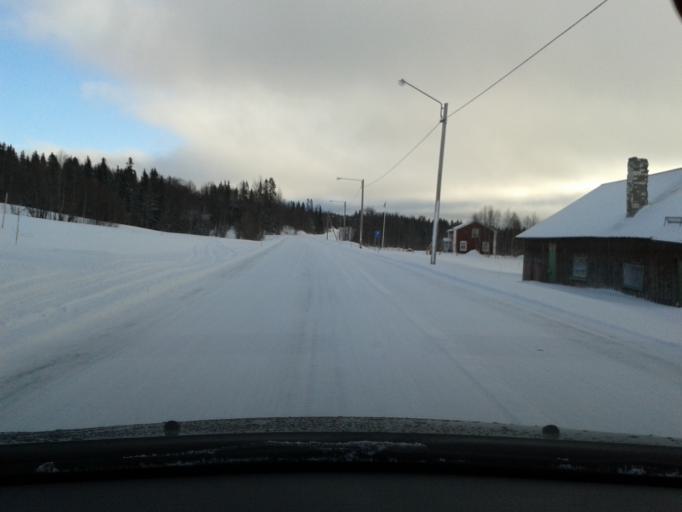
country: SE
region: Vaesterbotten
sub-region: Vilhelmina Kommun
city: Sjoberg
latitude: 65.2507
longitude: 15.5782
